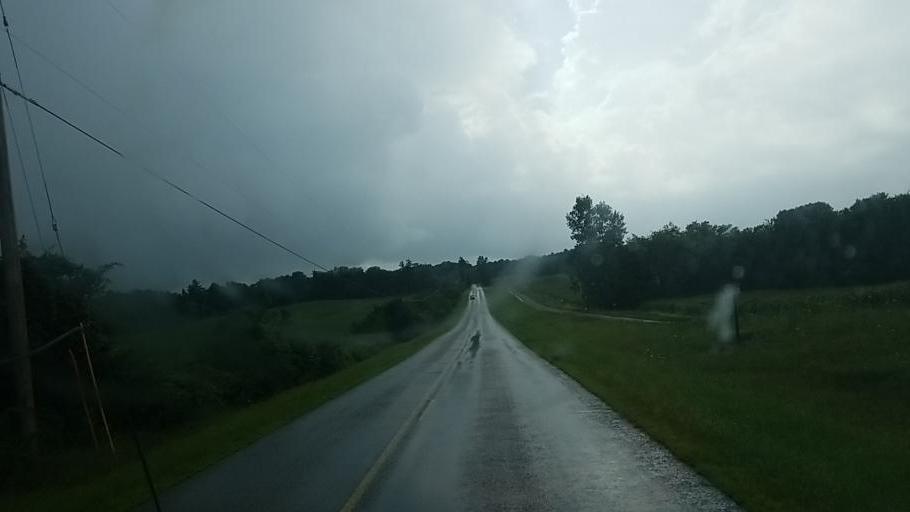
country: US
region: Ohio
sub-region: Champaign County
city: North Lewisburg
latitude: 40.3198
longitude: -83.6003
